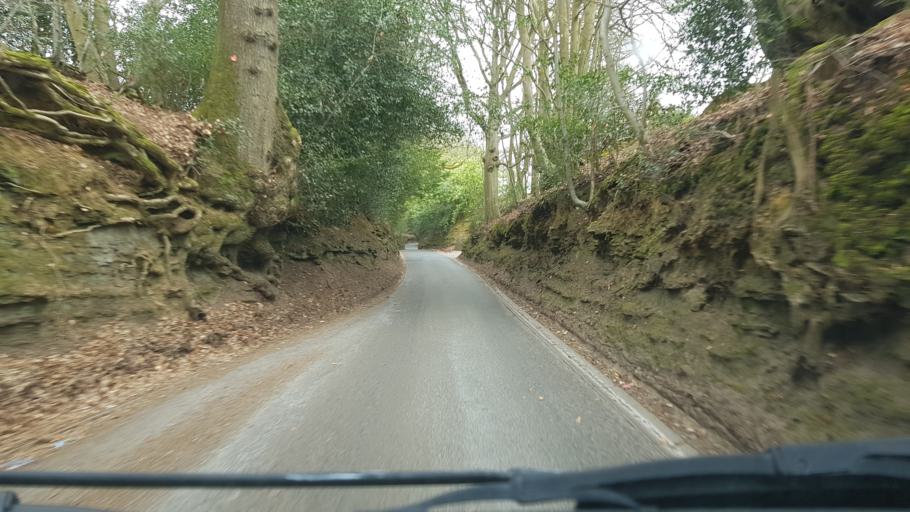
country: GB
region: England
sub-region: Surrey
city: Cranleigh
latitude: 51.1863
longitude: -0.4636
